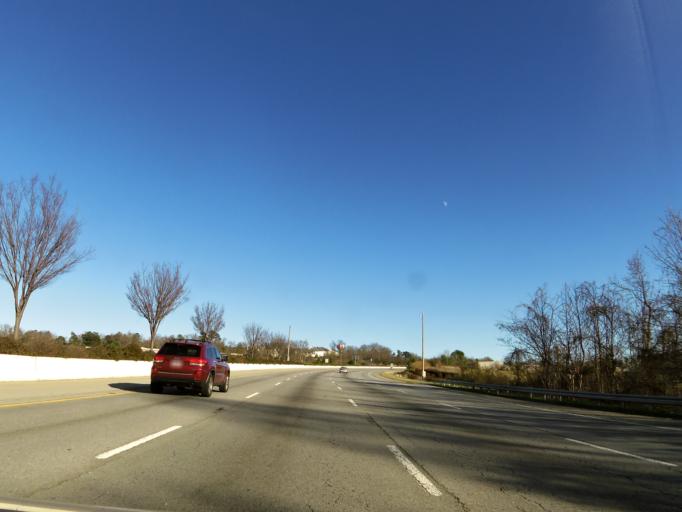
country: US
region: South Carolina
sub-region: Greenville County
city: Greenville
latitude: 34.8584
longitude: -82.3502
